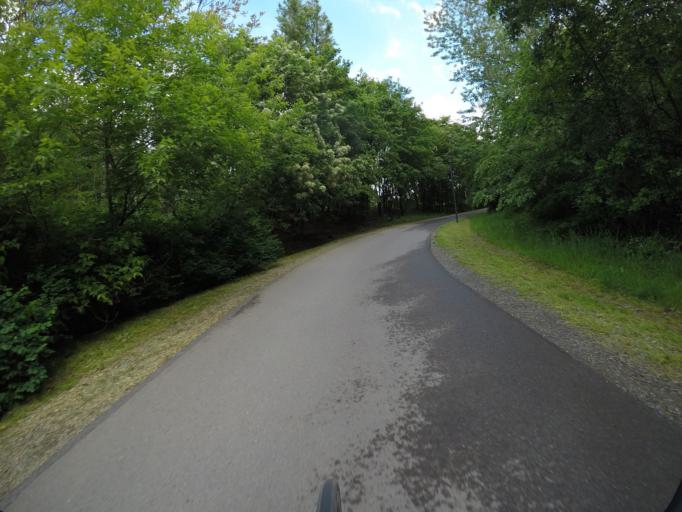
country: DE
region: Berlin
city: Marzahn
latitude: 52.5352
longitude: 13.5786
